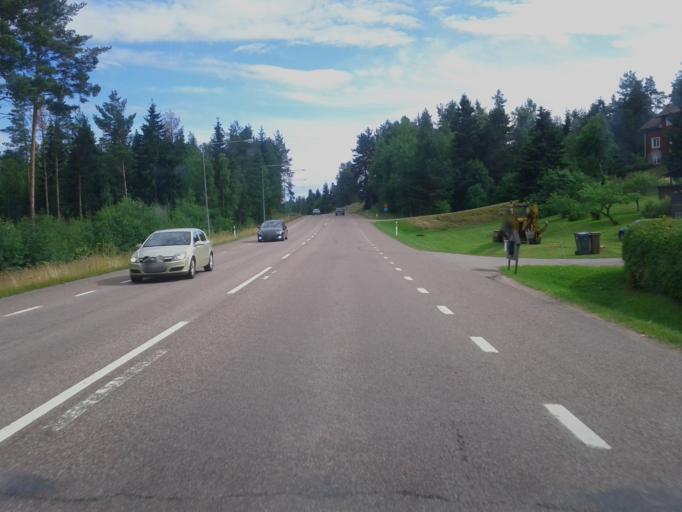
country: SE
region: Dalarna
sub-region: Faluns Kommun
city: Bjursas
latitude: 60.7319
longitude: 15.4402
